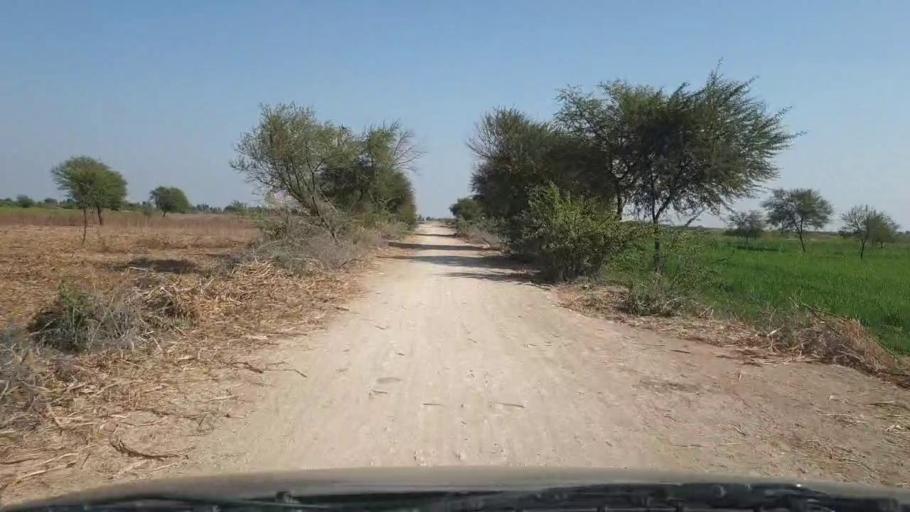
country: PK
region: Sindh
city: Samaro
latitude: 25.1972
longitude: 69.2723
